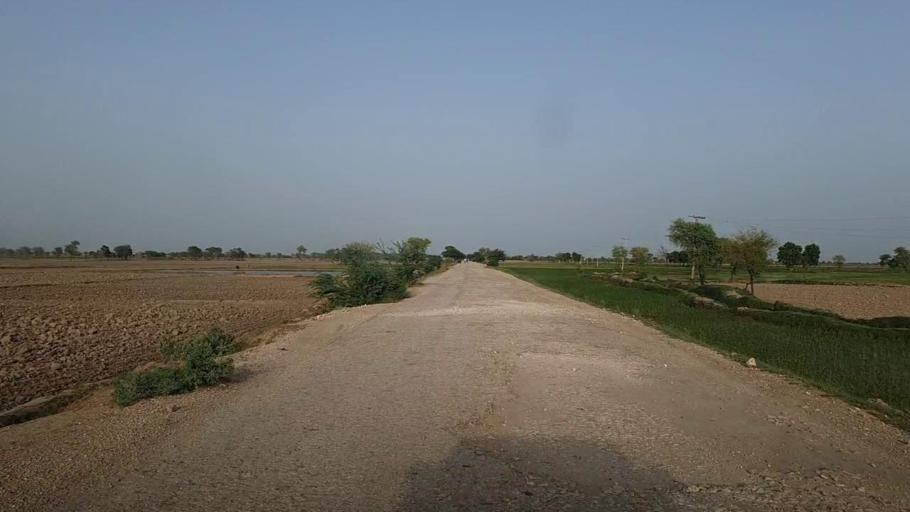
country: PK
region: Sindh
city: Mehar
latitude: 27.1647
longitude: 67.7816
